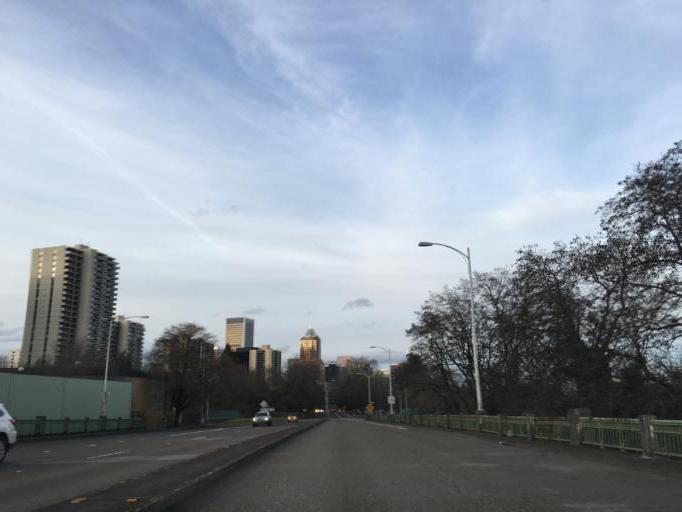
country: US
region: Oregon
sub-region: Multnomah County
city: Portland
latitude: 45.5040
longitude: -122.6777
